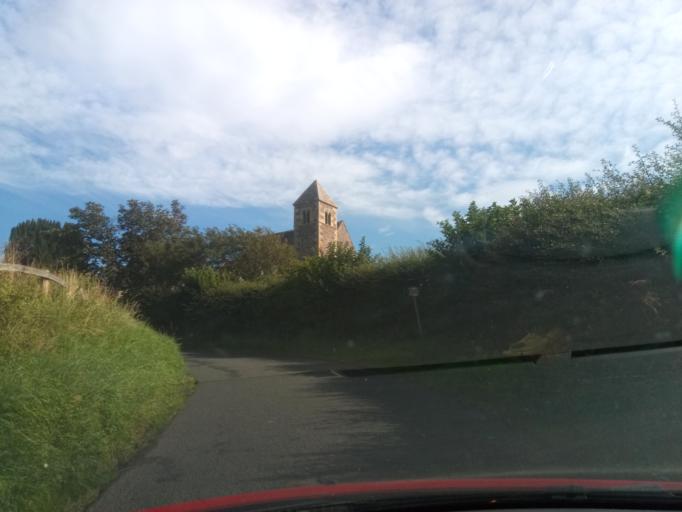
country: GB
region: Scotland
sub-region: The Scottish Borders
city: Coldstream
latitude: 55.6312
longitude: -2.1736
